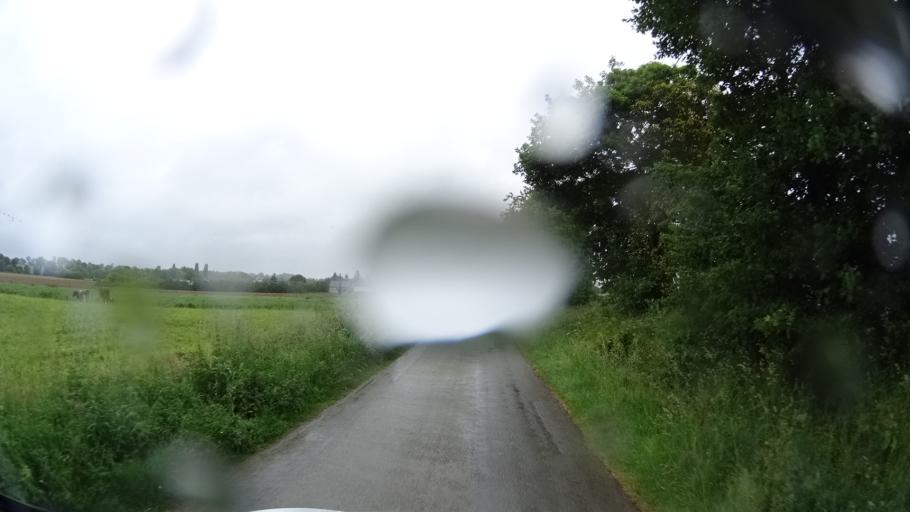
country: FR
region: Brittany
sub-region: Departement d'Ille-et-Vilaine
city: Vern-sur-Seiche
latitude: 48.0290
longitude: -1.6242
